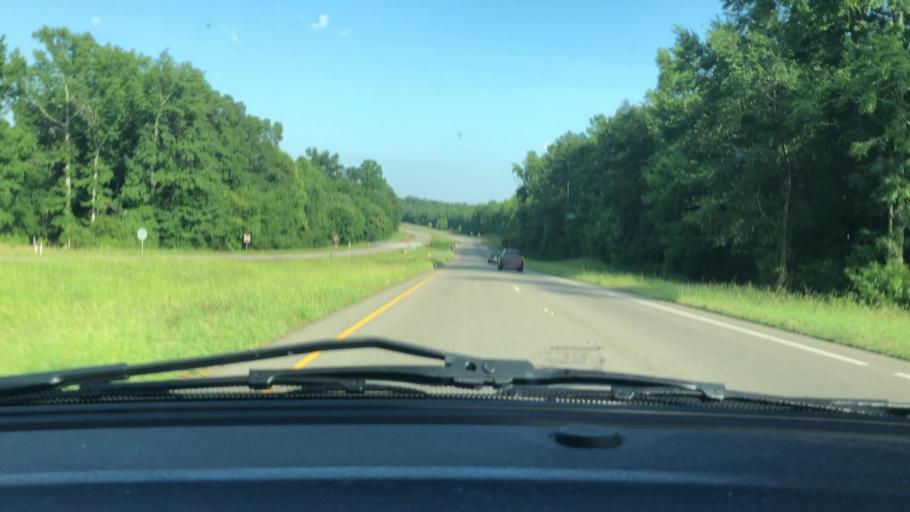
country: US
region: North Carolina
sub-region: Chatham County
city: Farmville
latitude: 35.6139
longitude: -79.3462
